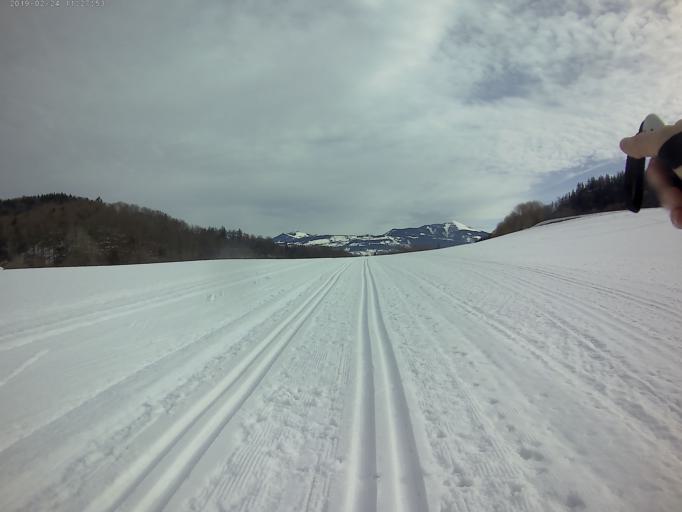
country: AT
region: Salzburg
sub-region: Politischer Bezirk Hallein
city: Hallein
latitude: 47.6758
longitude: 13.0698
